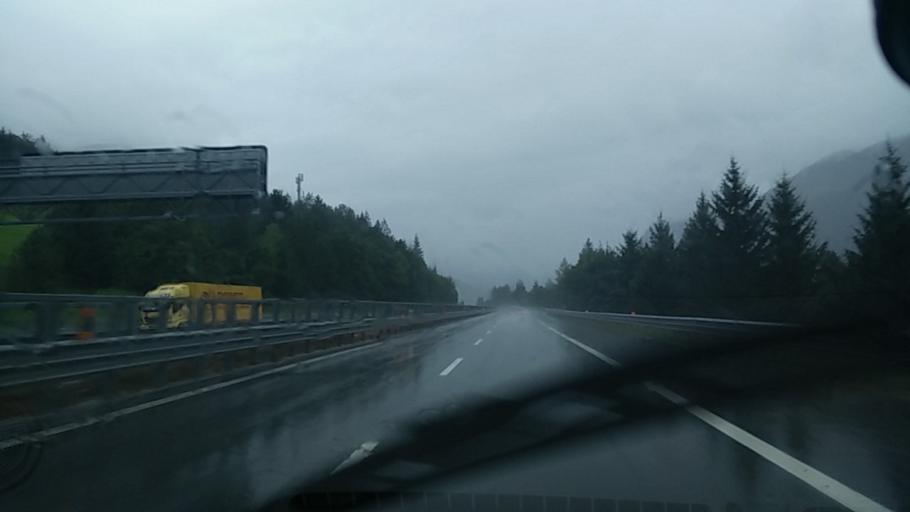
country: IT
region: Friuli Venezia Giulia
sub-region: Provincia di Udine
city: Malborghetto
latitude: 46.4982
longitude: 13.4111
